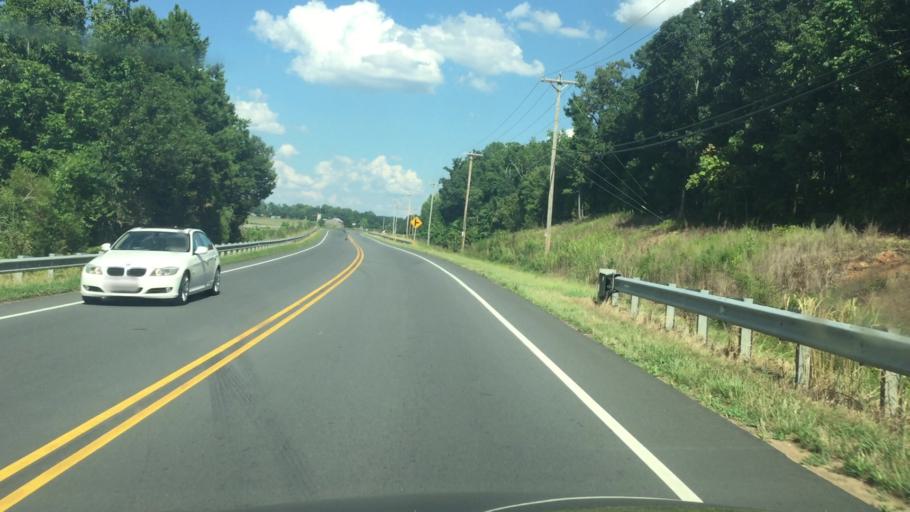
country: US
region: North Carolina
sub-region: Cabarrus County
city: Kannapolis
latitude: 35.4373
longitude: -80.7072
